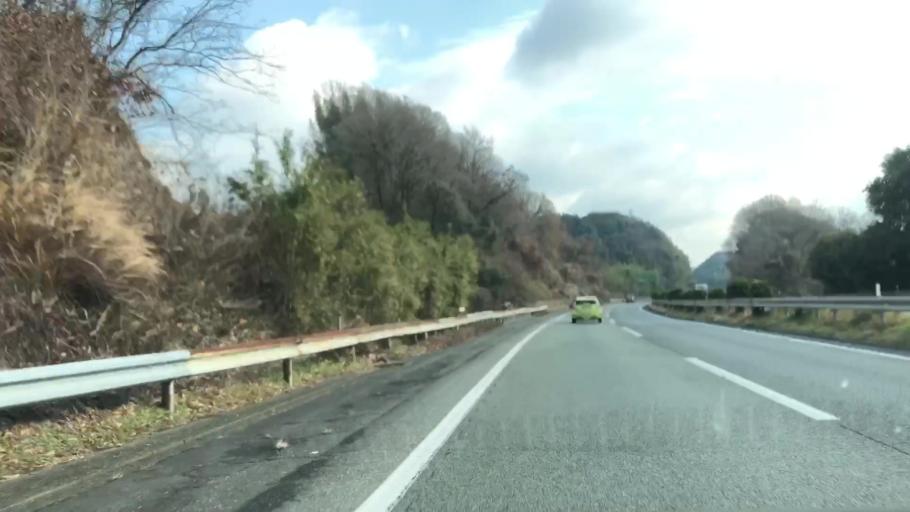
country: JP
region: Kumamoto
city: Tamana
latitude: 33.0015
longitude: 130.5884
